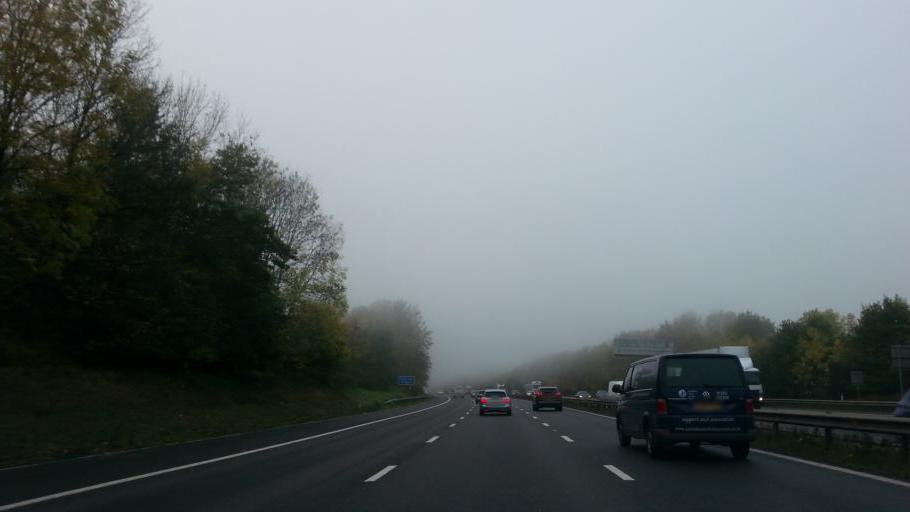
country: GB
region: England
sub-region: Worcestershire
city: Alvechurch
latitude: 52.3557
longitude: -1.9826
